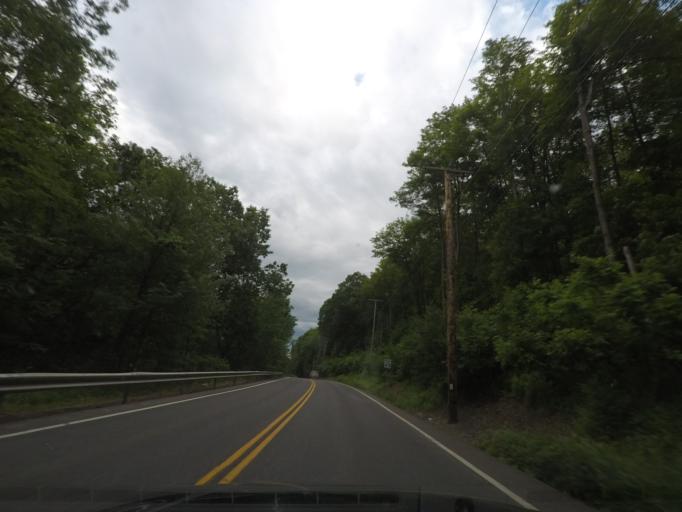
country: US
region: New York
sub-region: Dutchess County
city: Pine Plains
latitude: 41.9706
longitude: -73.7355
